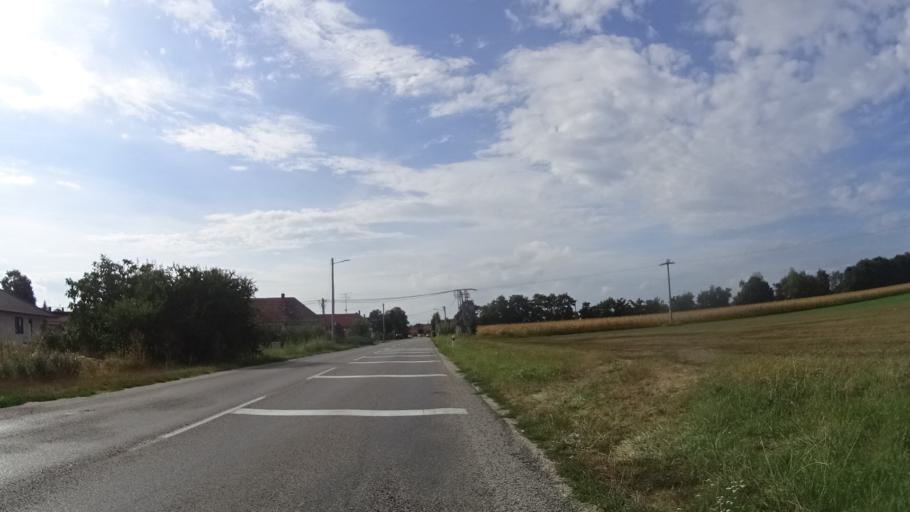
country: SK
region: Trnavsky
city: Gabcikovo
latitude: 47.9169
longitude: 17.5045
